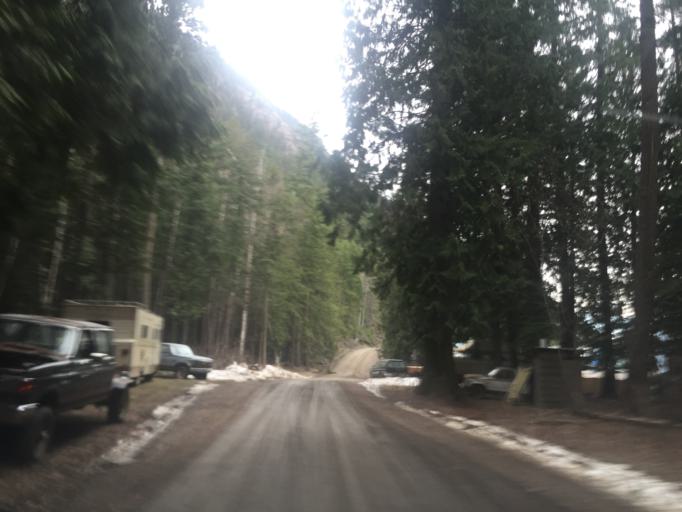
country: CA
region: British Columbia
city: Chase
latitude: 51.4119
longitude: -120.1280
